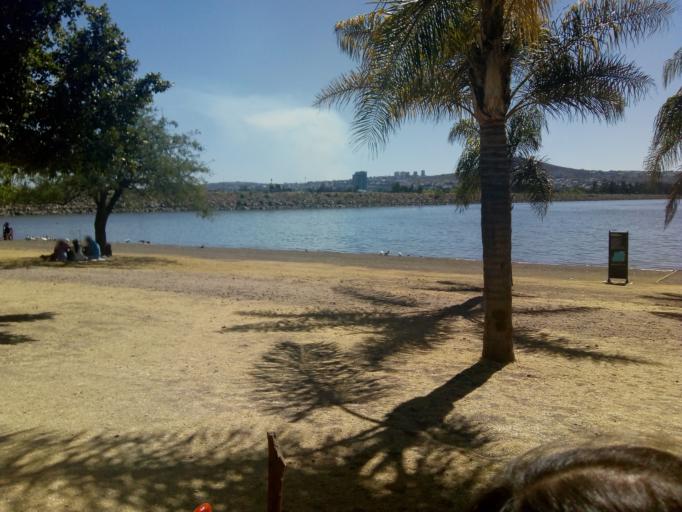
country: MX
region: Guanajuato
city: Leon
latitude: 21.1748
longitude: -101.6794
